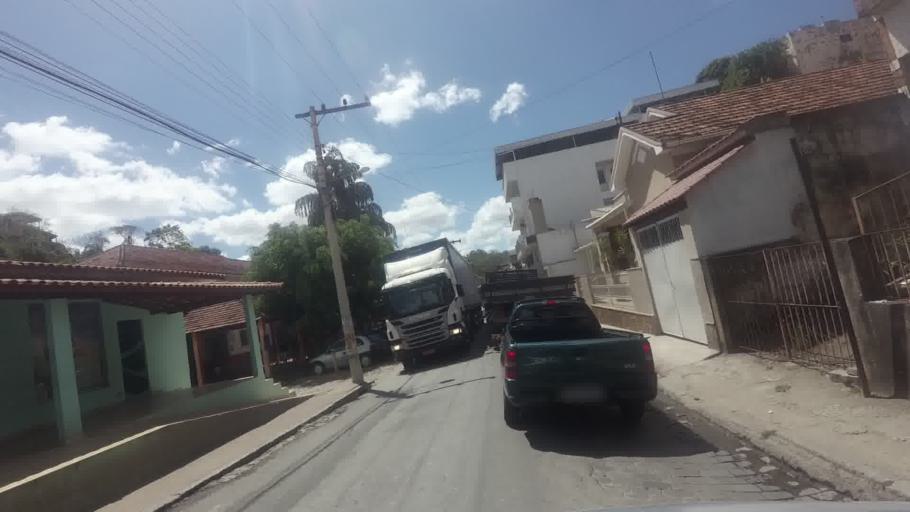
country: BR
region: Minas Gerais
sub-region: Recreio
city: Recreio
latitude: -21.6587
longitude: -42.3466
